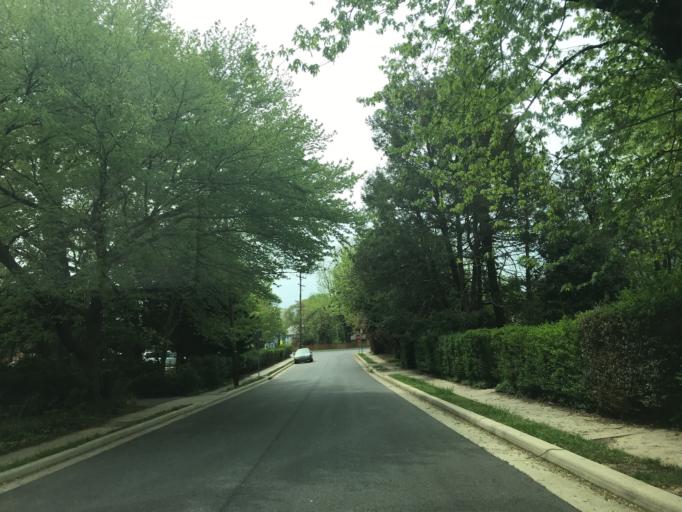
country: US
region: Maryland
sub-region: Baltimore County
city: Catonsville
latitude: 39.2709
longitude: -76.7416
